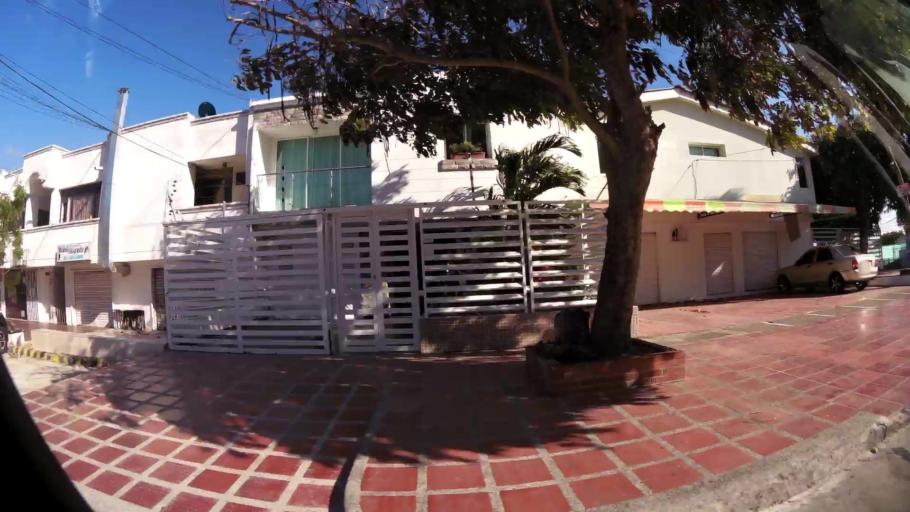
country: CO
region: Atlantico
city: Barranquilla
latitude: 10.9923
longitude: -74.8259
